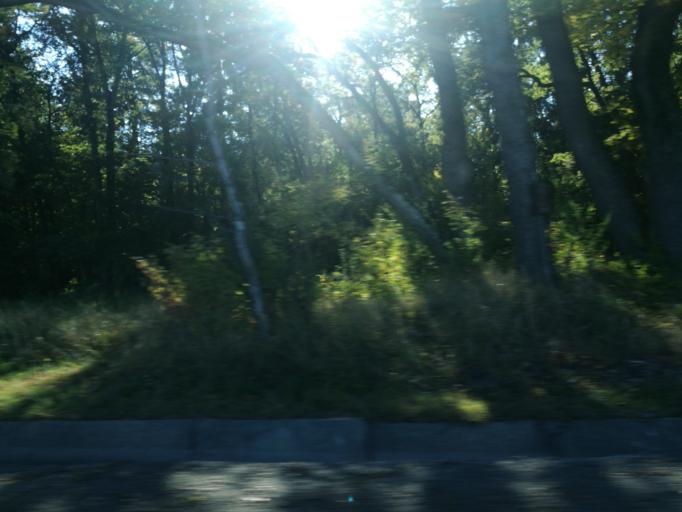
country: RO
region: Brasov
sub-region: Comuna Dumbravita
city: Dumbravita
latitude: 45.7356
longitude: 25.4367
